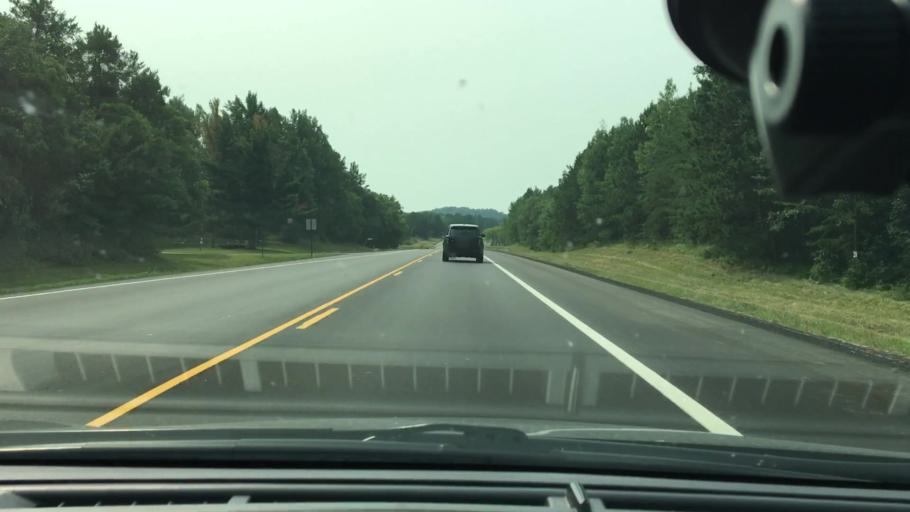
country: US
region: Minnesota
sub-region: Crow Wing County
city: Brainerd
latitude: 46.4089
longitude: -94.1760
